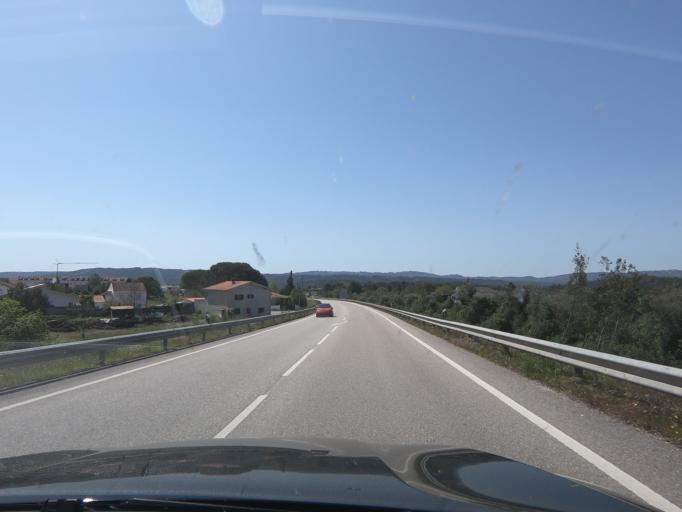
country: PT
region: Coimbra
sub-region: Lousa
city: Lousa
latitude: 40.1274
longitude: -8.2409
